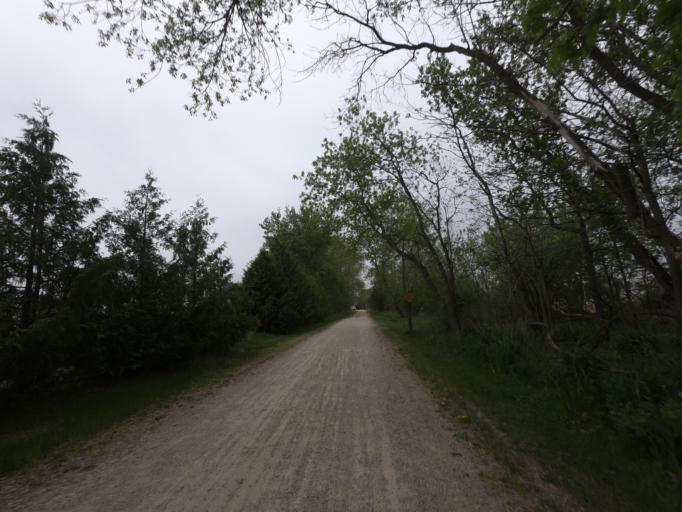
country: US
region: Wisconsin
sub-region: Jefferson County
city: Lake Mills
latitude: 43.0643
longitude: -88.9119
